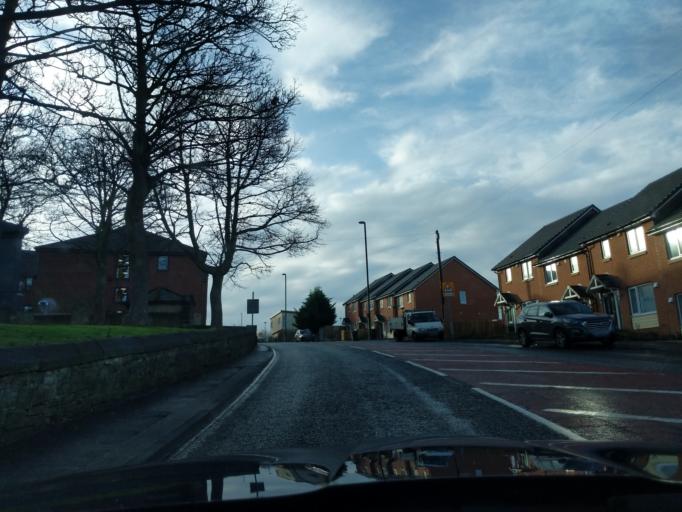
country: GB
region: England
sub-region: Borough of North Tyneside
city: Wallsend
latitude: 54.9952
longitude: -1.5168
